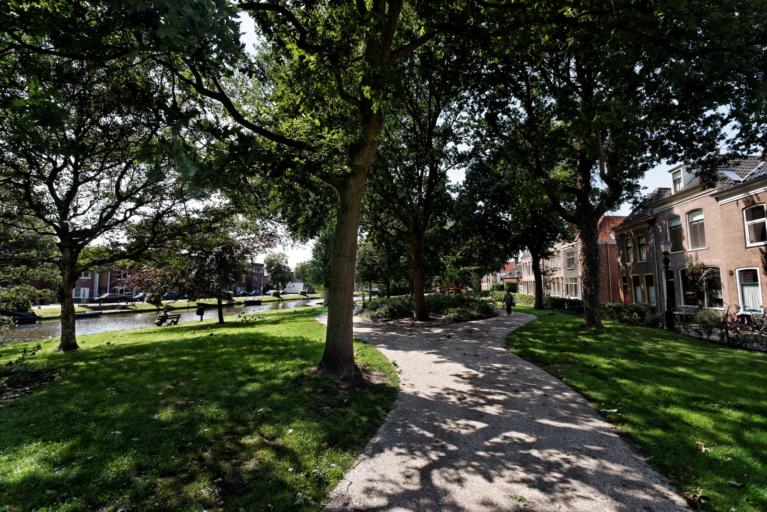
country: NL
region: North Holland
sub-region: Gemeente Alkmaar
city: Alkmaar
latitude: 52.6268
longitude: 4.7526
